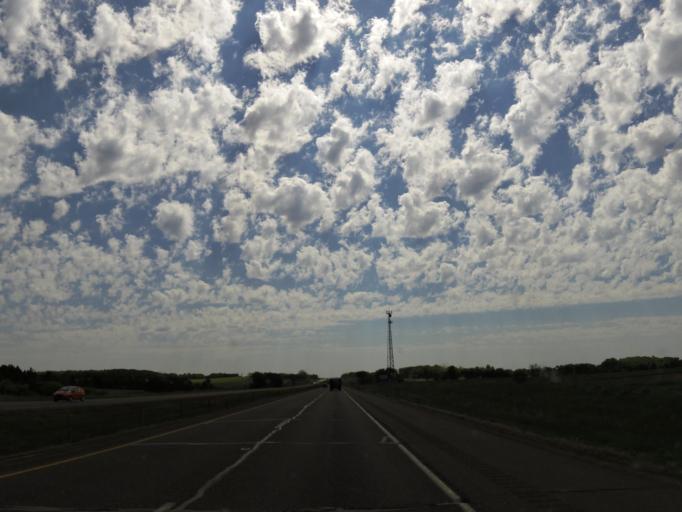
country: US
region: Wisconsin
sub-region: Dunn County
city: Colfax
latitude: 44.8618
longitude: -91.6749
